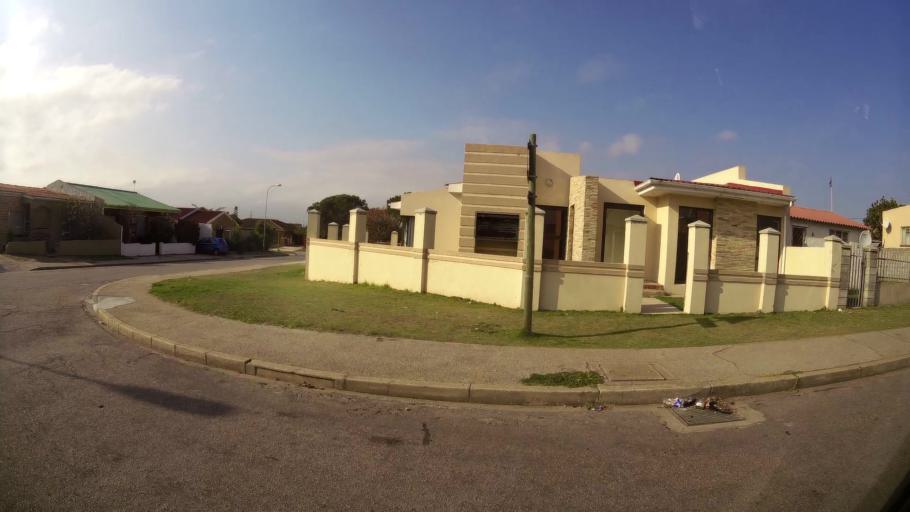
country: ZA
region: Eastern Cape
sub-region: Nelson Mandela Bay Metropolitan Municipality
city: Port Elizabeth
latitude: -33.9224
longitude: 25.5589
